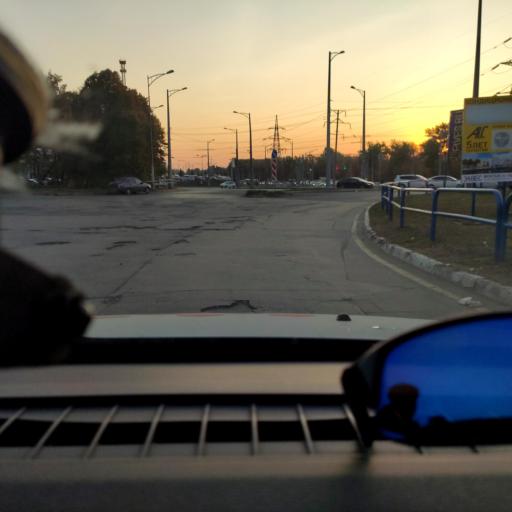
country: RU
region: Samara
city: Samara
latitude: 53.2164
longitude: 50.1881
